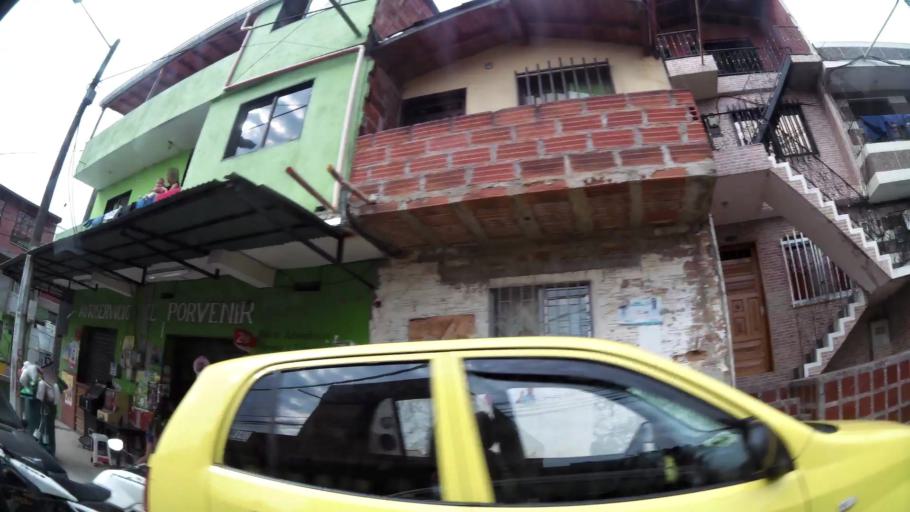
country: CO
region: Antioquia
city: Bello
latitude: 6.3000
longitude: -75.5515
